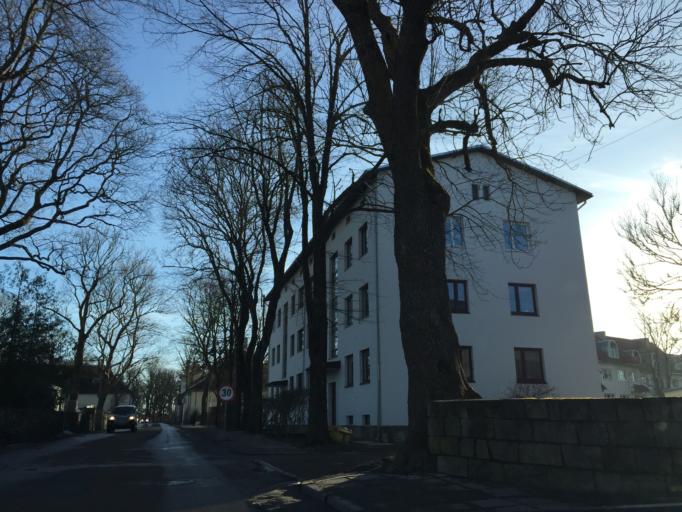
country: EE
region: Saare
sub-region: Kuressaare linn
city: Kuressaare
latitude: 58.2519
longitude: 22.4796
